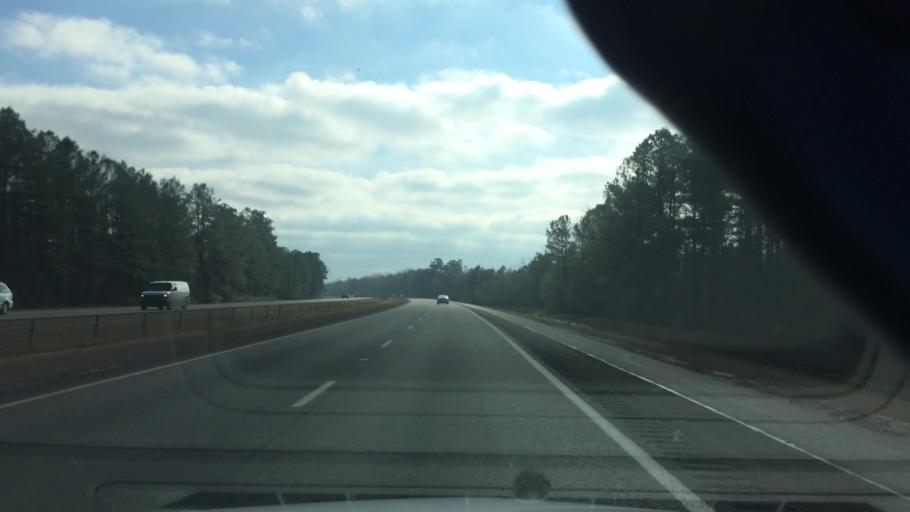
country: US
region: North Carolina
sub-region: Pender County
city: Rocky Point
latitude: 34.4657
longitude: -77.8803
